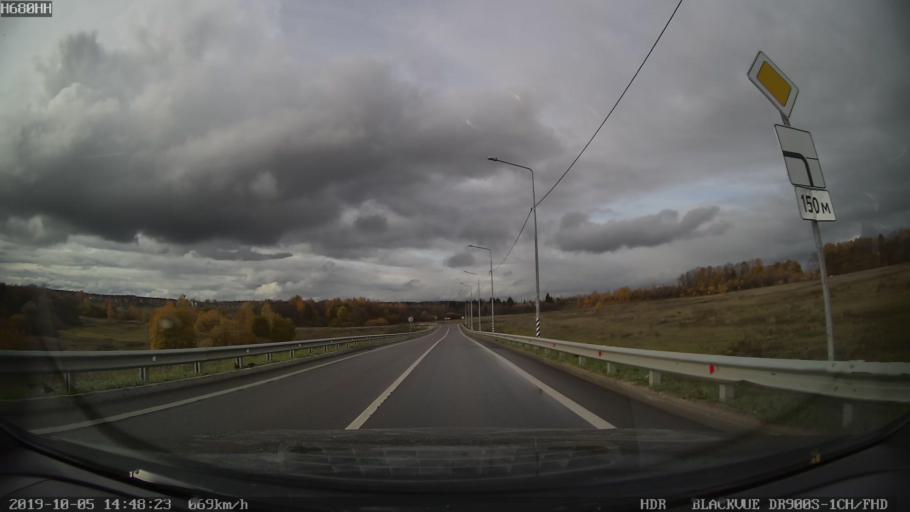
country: RU
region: Moskovskaya
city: Solnechnogorsk
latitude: 56.2148
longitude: 36.9007
